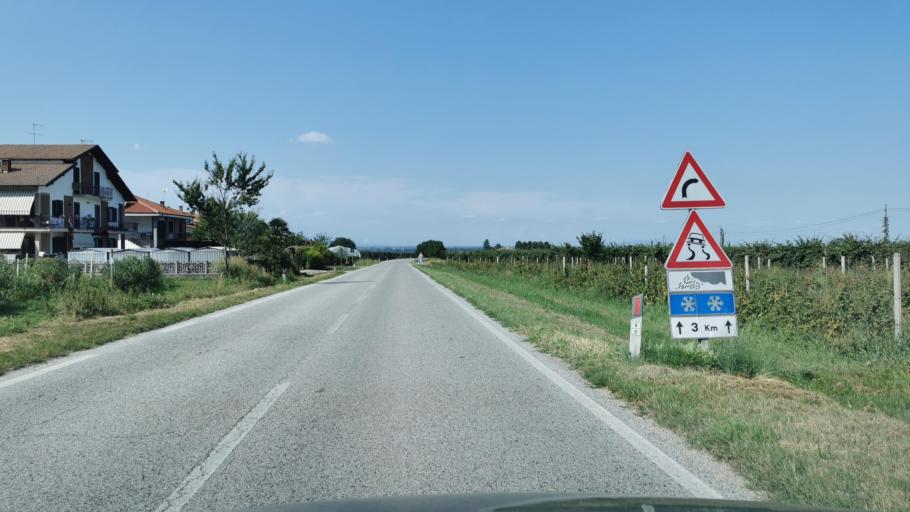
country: IT
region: Piedmont
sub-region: Provincia di Cuneo
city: Revello
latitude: 44.6611
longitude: 7.3940
